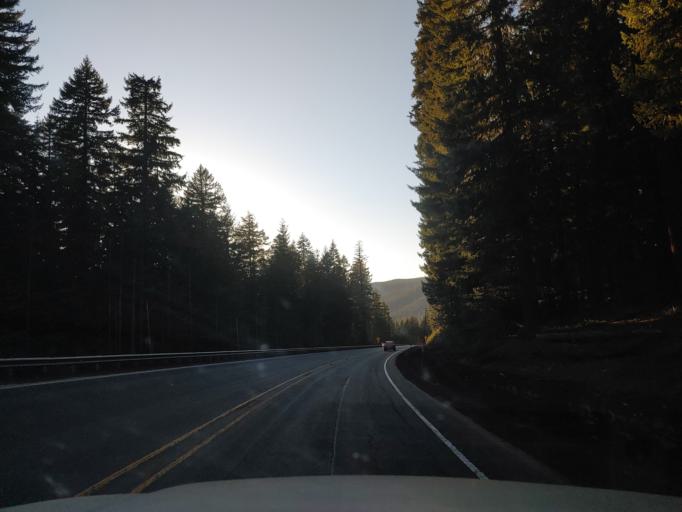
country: US
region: Oregon
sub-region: Lane County
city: Oakridge
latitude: 43.6120
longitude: -122.0645
